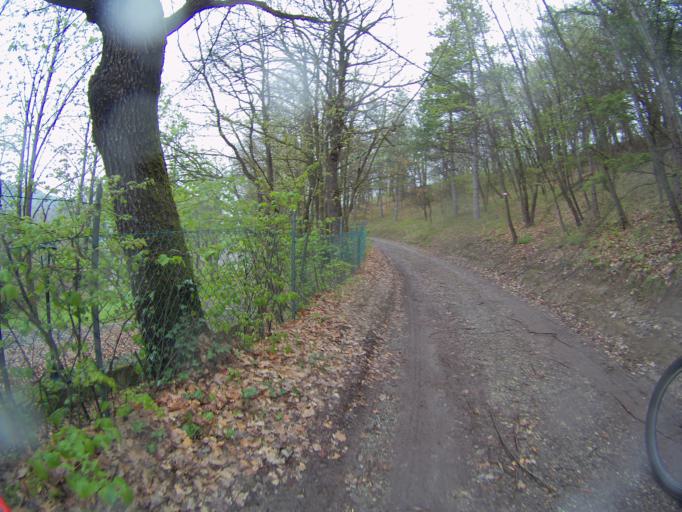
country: IT
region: Emilia-Romagna
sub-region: Provincia di Reggio Emilia
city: Ciano d'Enza
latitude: 44.5679
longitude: 10.4076
